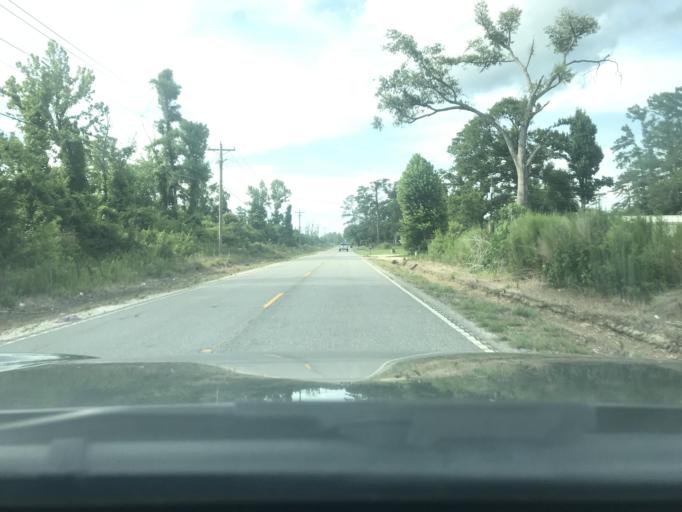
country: US
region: Louisiana
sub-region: Calcasieu Parish
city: Moss Bluff
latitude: 30.3165
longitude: -93.2583
